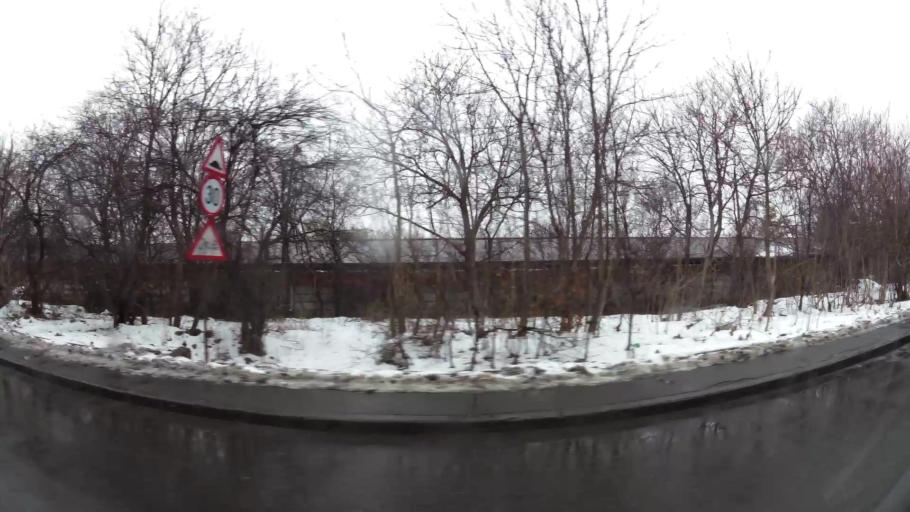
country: RO
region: Ilfov
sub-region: Comuna Chiajna
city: Rosu
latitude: 44.4860
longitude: 26.0585
